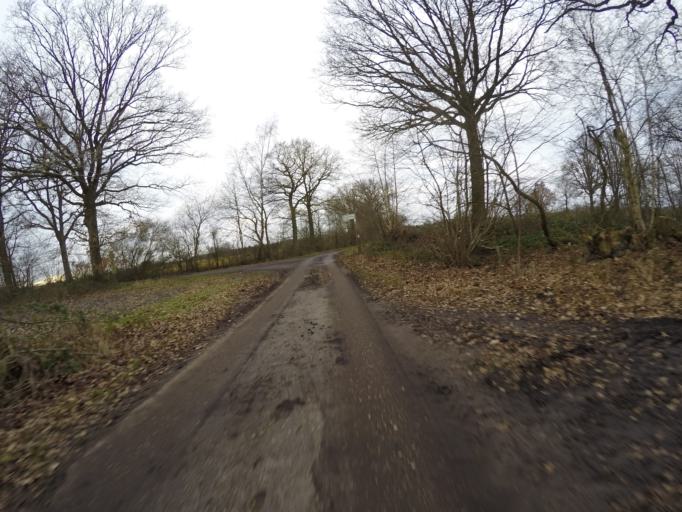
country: DE
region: Schleswig-Holstein
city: Hemdingen
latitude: 53.7848
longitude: 9.8354
